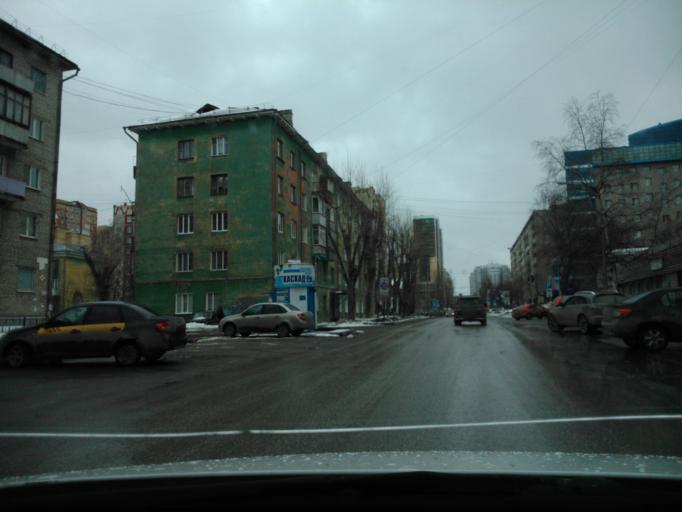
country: RU
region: Perm
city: Perm
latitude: 58.0048
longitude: 56.2625
